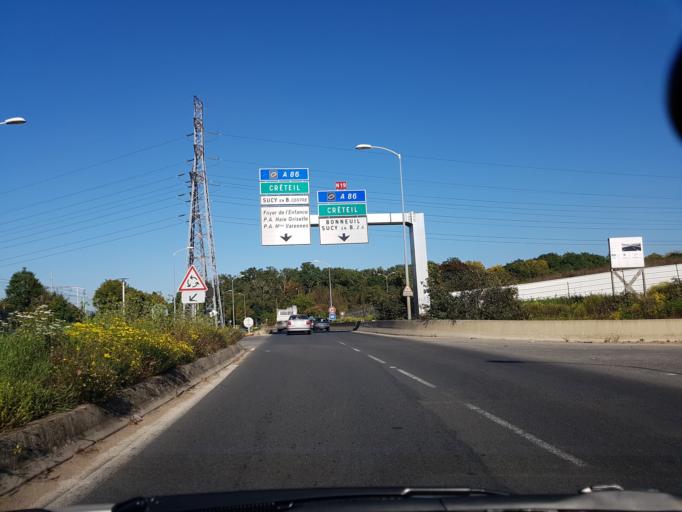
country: FR
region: Ile-de-France
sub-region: Departement du Val-de-Marne
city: Boissy-Saint-Leger
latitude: 48.7548
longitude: 2.5067
